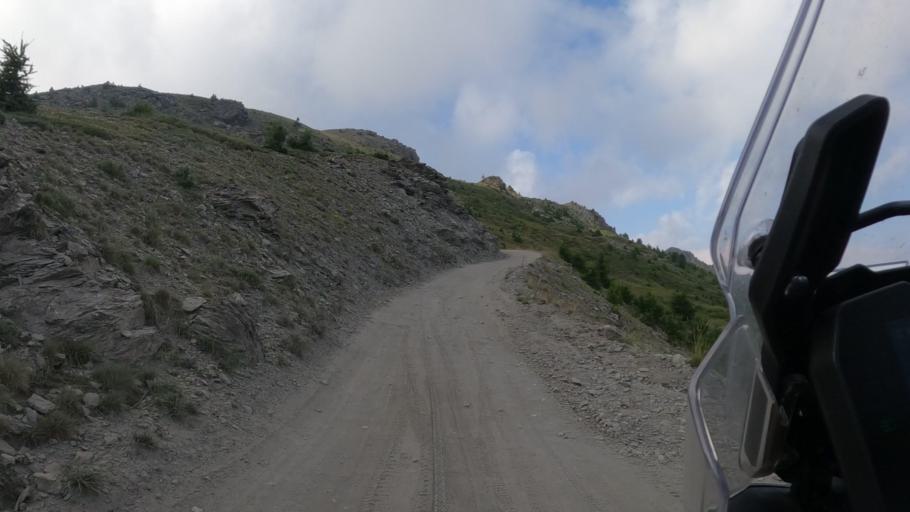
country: IT
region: Piedmont
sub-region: Provincia di Torino
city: Pragelato-Rua
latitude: 45.0352
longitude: 6.9081
